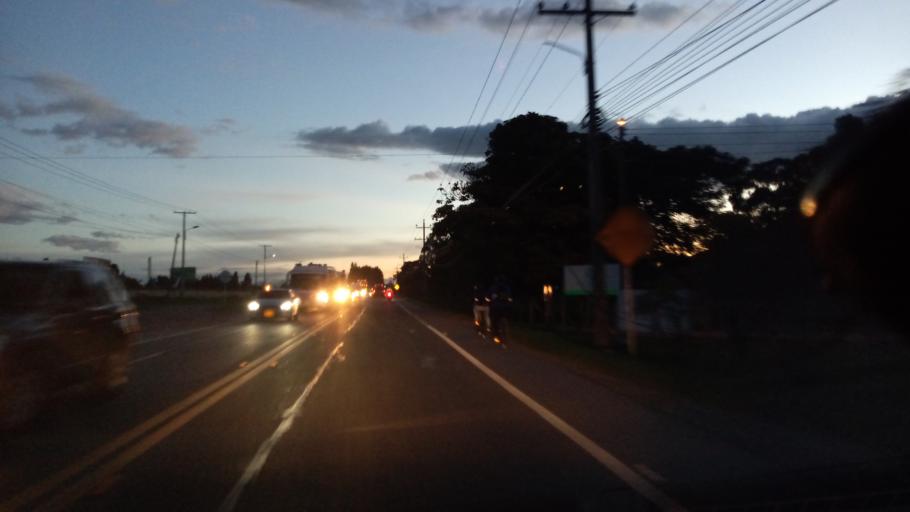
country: CO
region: Cundinamarca
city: Cota
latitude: 4.8324
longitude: -74.0888
